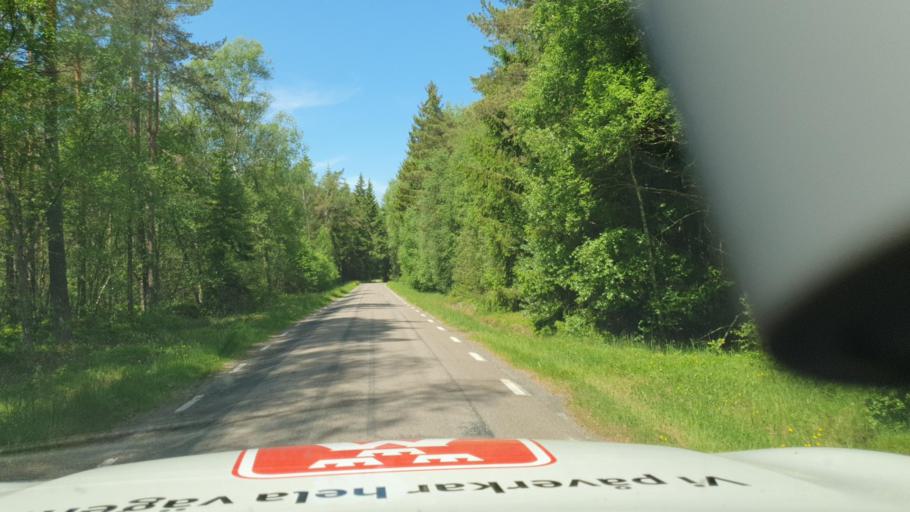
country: SE
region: Vaestra Goetaland
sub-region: Herrljunga Kommun
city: Herrljunga
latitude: 58.1272
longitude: 13.0866
